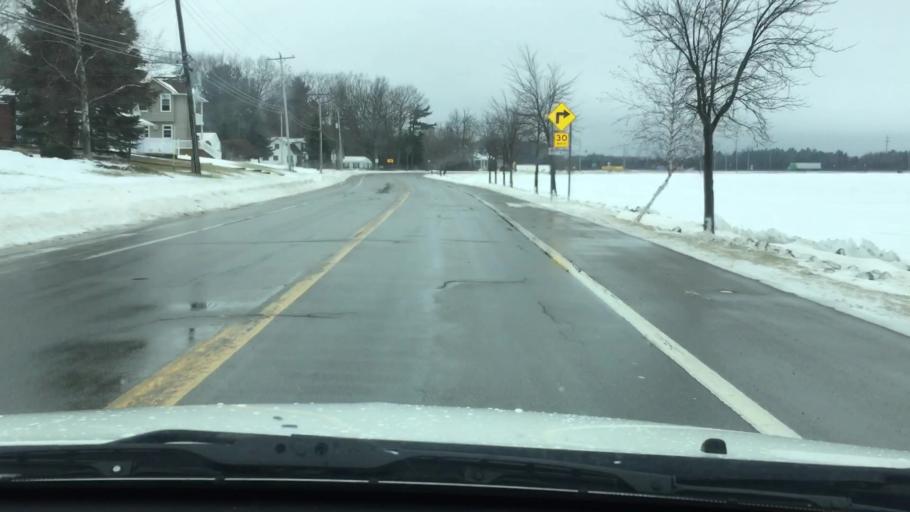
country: US
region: Michigan
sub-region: Wexford County
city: Cadillac
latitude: 44.2318
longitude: -85.4412
